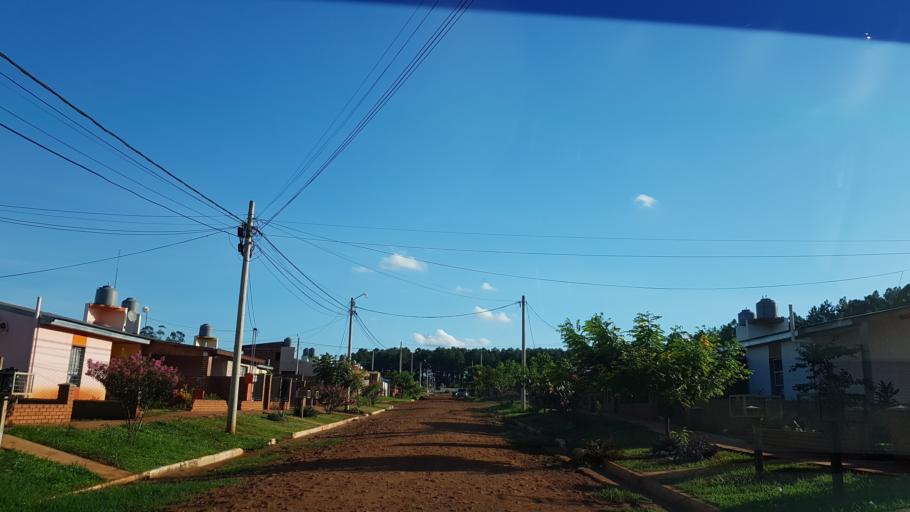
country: AR
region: Misiones
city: Puerto Libertad
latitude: -25.9172
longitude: -54.5900
